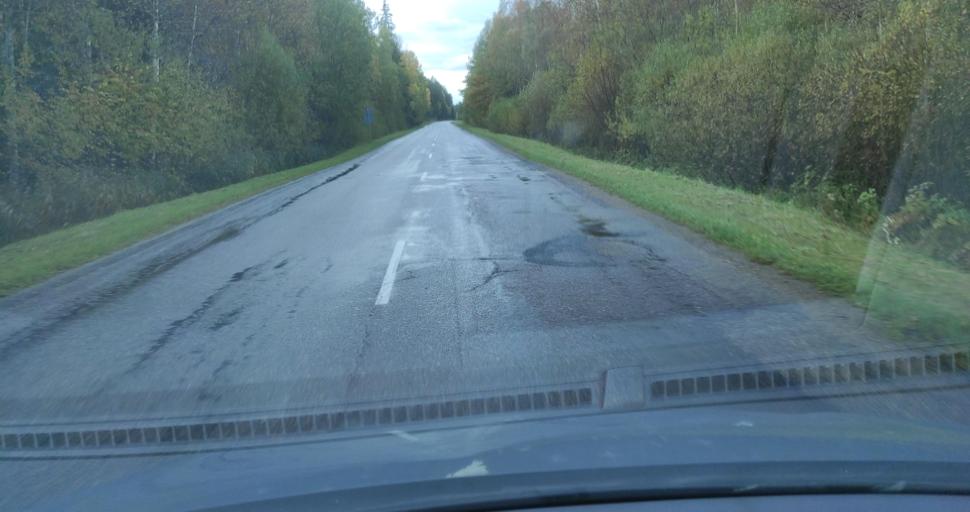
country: LV
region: Skrunda
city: Skrunda
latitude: 56.6575
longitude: 22.0202
